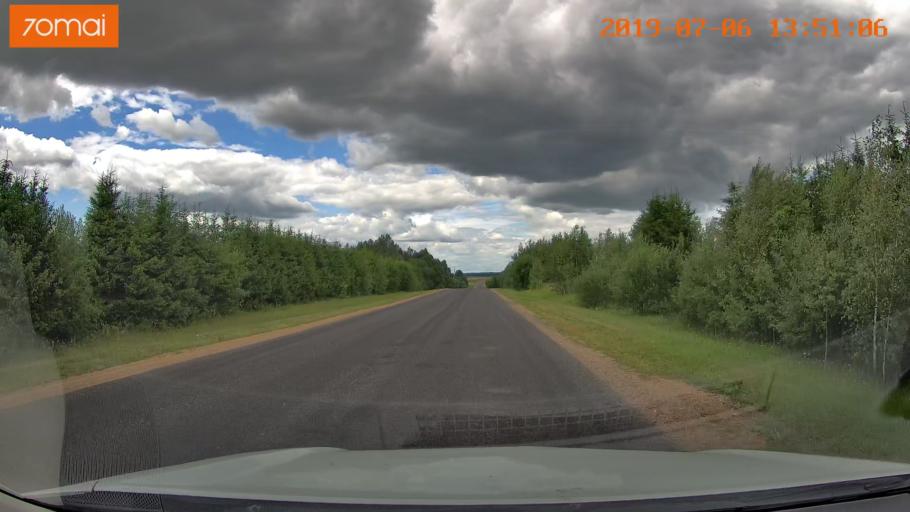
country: BY
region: Minsk
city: Ivyanyets
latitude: 53.7049
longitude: 26.8364
